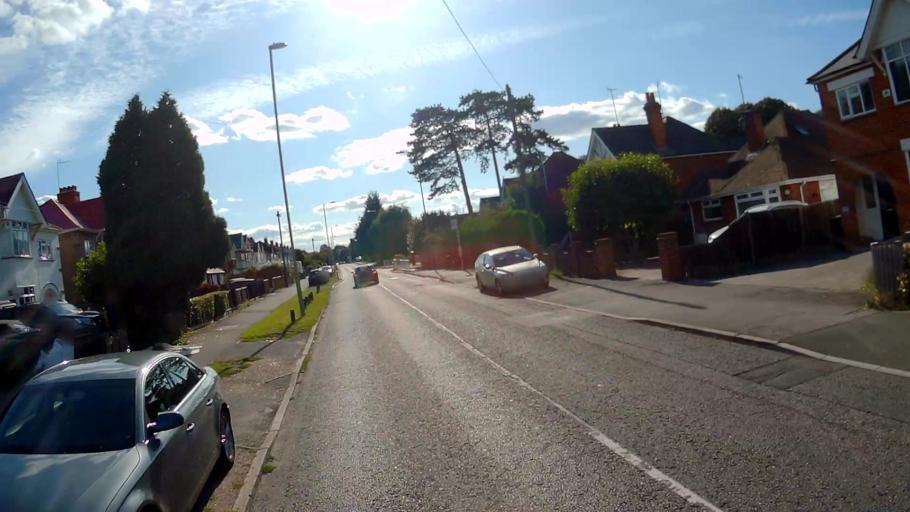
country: GB
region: England
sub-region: Hampshire
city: Basingstoke
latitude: 51.2576
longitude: -1.0987
